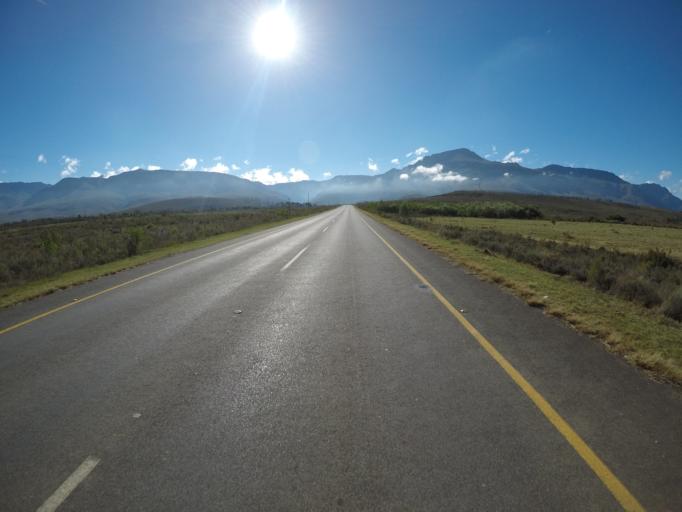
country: ZA
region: Western Cape
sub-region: Overberg District Municipality
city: Caledon
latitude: -34.0605
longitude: 19.5582
